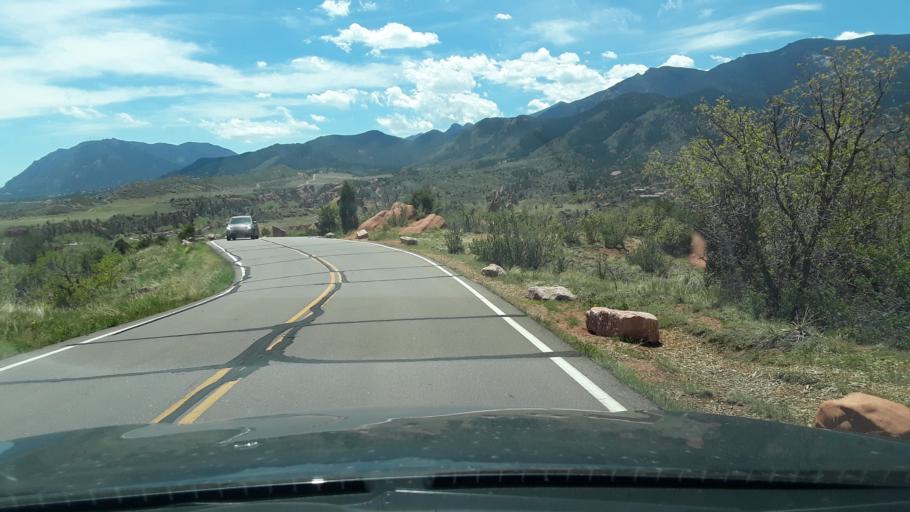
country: US
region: Colorado
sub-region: El Paso County
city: Manitou Springs
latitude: 38.8623
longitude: -104.8789
